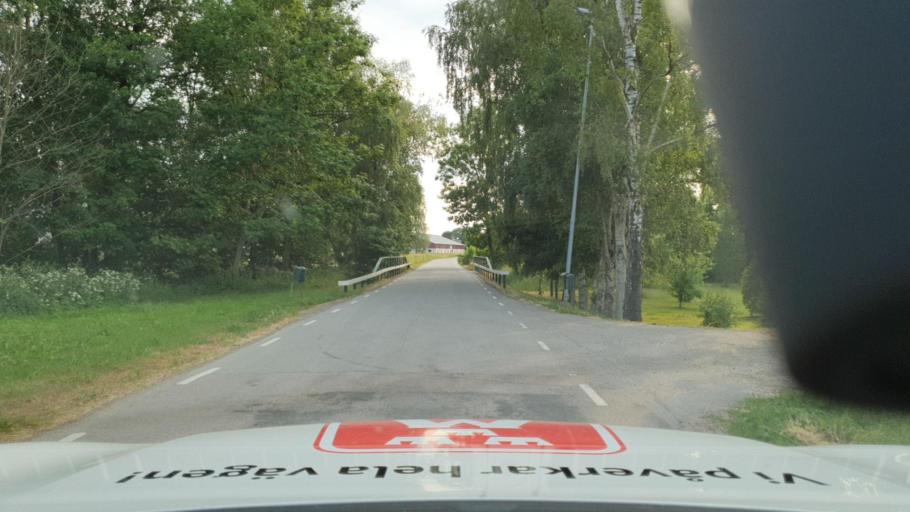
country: SE
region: Skane
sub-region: Sjobo Kommun
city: Sjoebo
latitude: 55.6432
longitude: 13.8291
